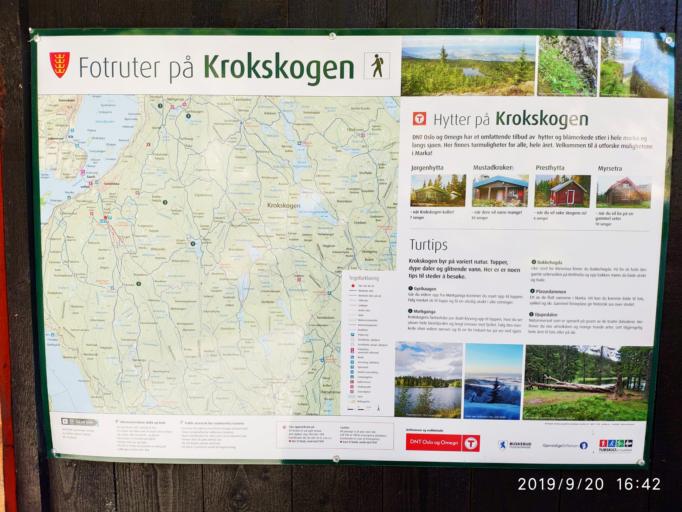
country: NO
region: Buskerud
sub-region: Hole
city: Vik
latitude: 60.0468
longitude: 10.3226
